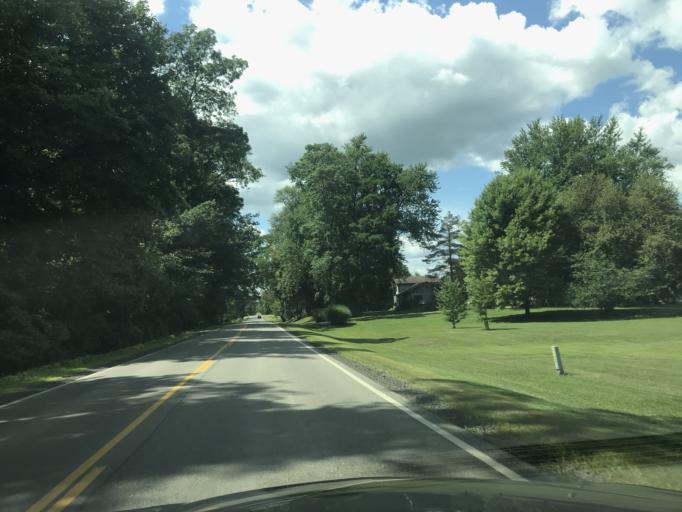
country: US
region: Michigan
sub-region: Ingham County
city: Leslie
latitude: 42.4510
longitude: -84.5290
